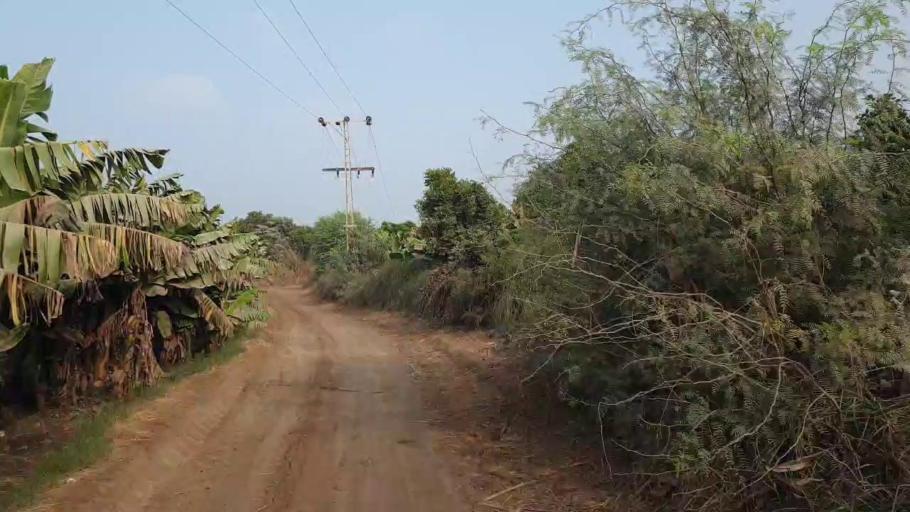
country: PK
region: Sindh
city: Tando Muhammad Khan
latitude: 25.1606
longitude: 68.5843
